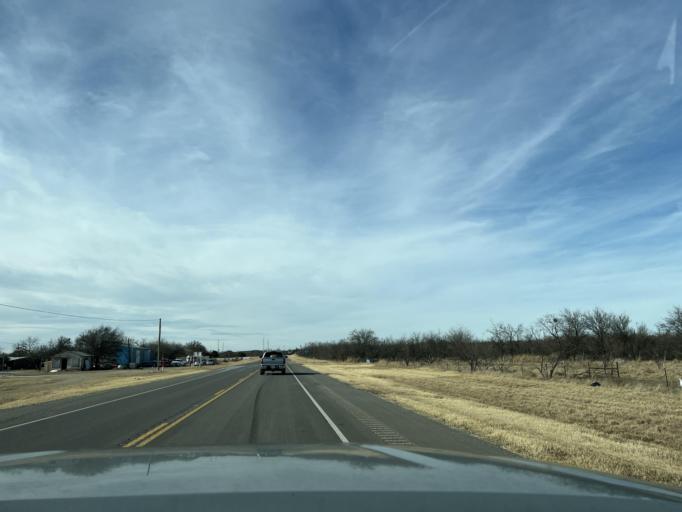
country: US
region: Texas
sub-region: Shackelford County
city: Albany
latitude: 32.7181
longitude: -99.2869
